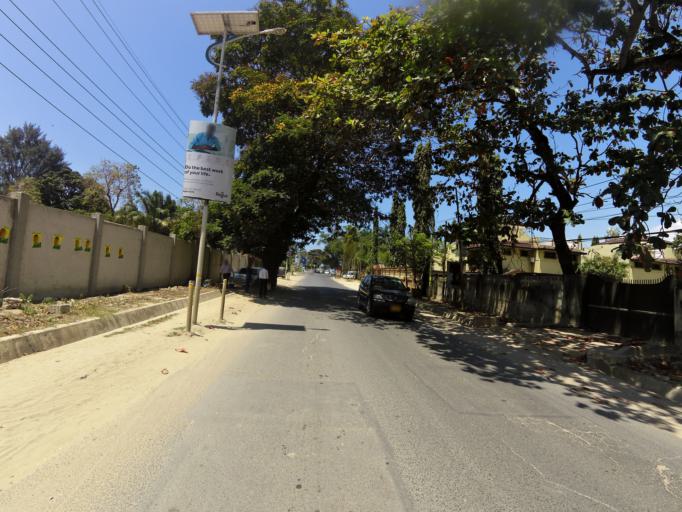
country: TZ
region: Dar es Salaam
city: Magomeni
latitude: -6.7908
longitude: 39.2776
